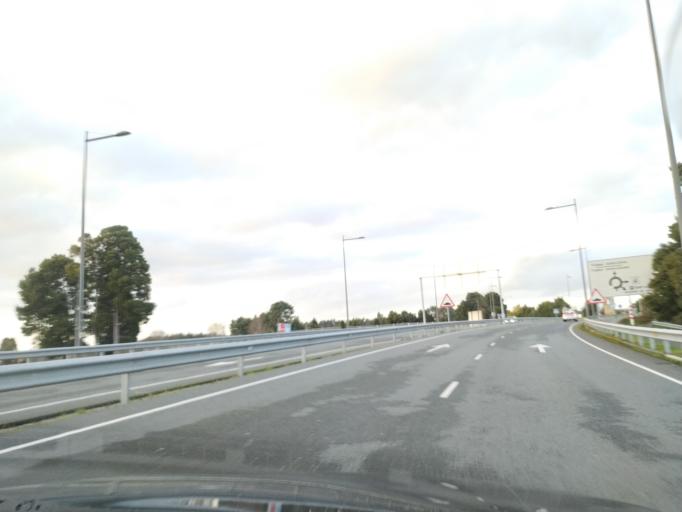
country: ES
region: Galicia
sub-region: Provincia da Coruna
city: Oroso
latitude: 42.8976
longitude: -8.4245
